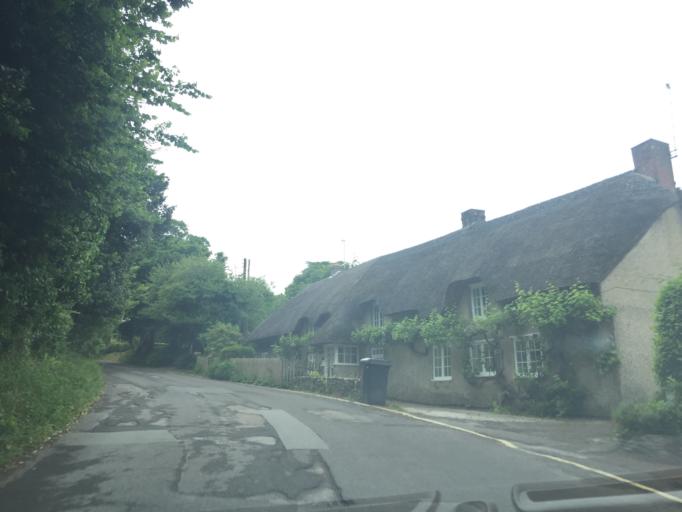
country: GB
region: England
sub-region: Dorset
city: Swanage
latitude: 50.6441
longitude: -1.9521
